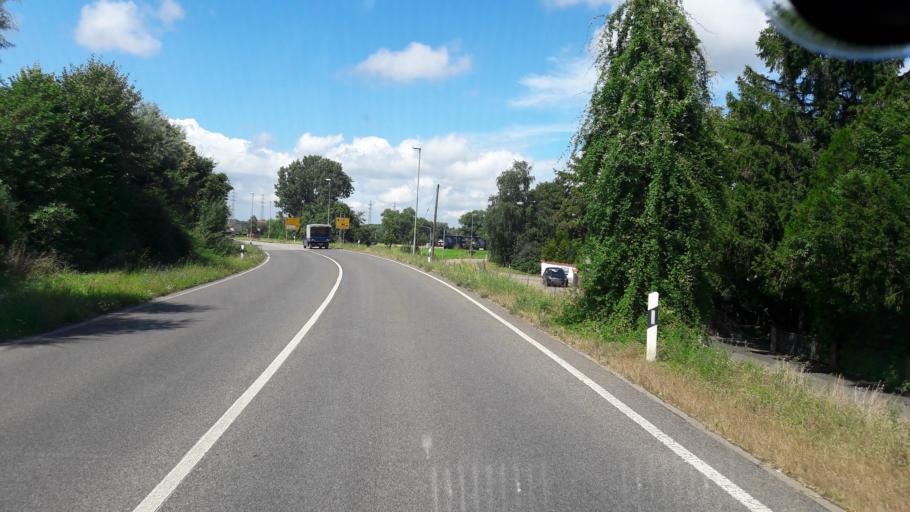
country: DE
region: Baden-Wuerttemberg
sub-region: Karlsruhe Region
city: Philippsburg
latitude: 49.2301
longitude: 8.4672
